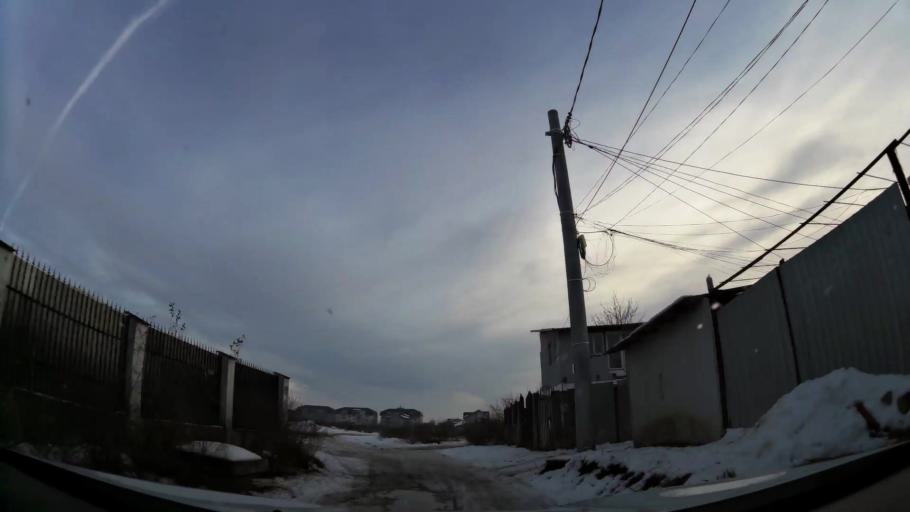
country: RO
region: Ilfov
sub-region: Comuna Magurele
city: Magurele
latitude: 44.3819
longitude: 26.0516
